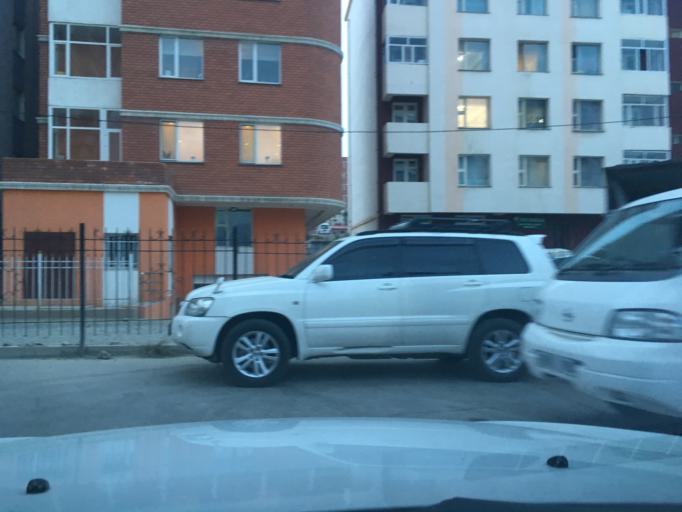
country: MN
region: Ulaanbaatar
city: Ulaanbaatar
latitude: 47.9172
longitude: 106.8597
